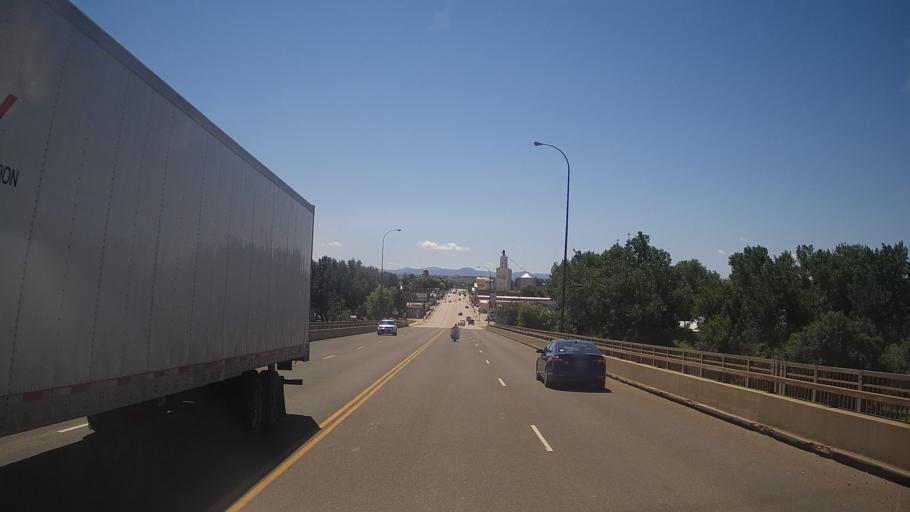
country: US
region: South Dakota
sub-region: Butte County
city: Belle Fourche
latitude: 44.6762
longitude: -103.8536
